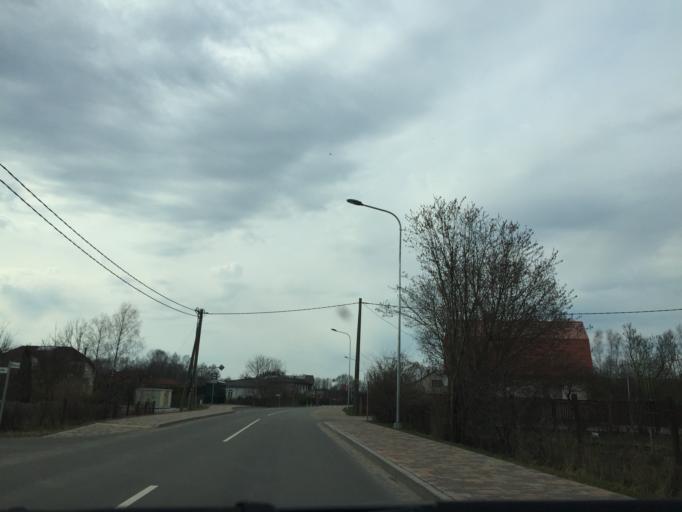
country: LV
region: Kekava
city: Balozi
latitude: 56.8853
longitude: 24.1624
